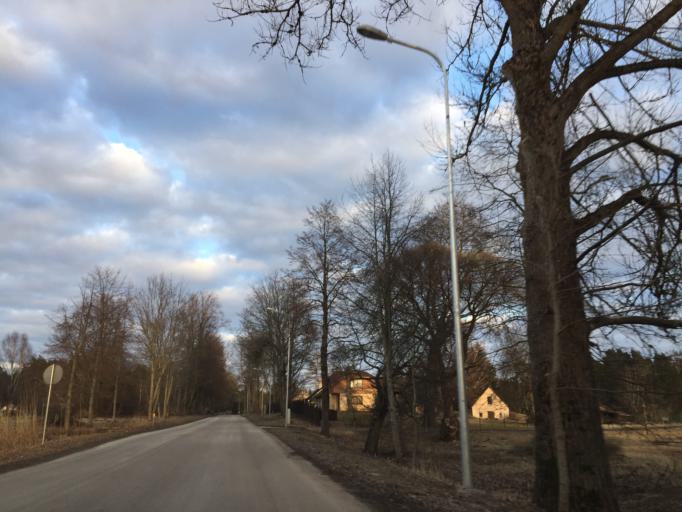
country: LV
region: Babite
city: Pinki
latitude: 56.9206
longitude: 23.8732
